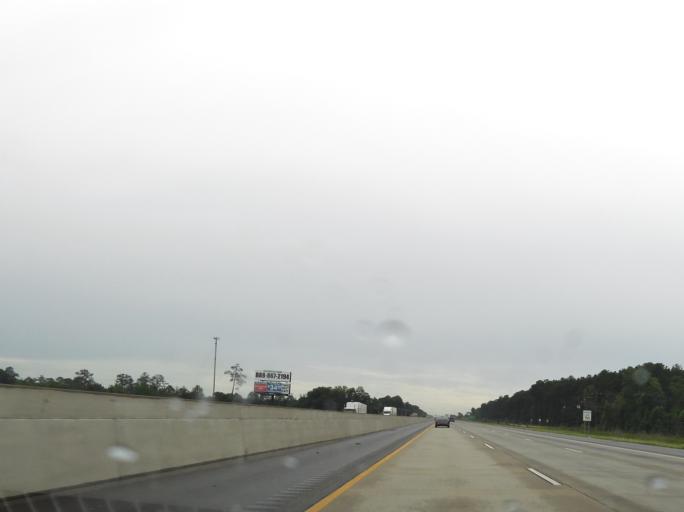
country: US
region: Georgia
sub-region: Cook County
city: Sparks
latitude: 31.2502
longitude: -83.4680
